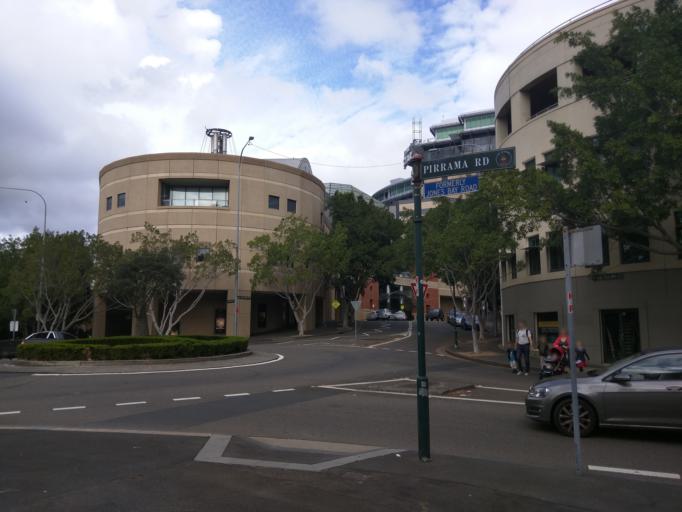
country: AU
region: New South Wales
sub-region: Leichhardt
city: Balmain East
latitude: -33.8662
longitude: 151.1949
